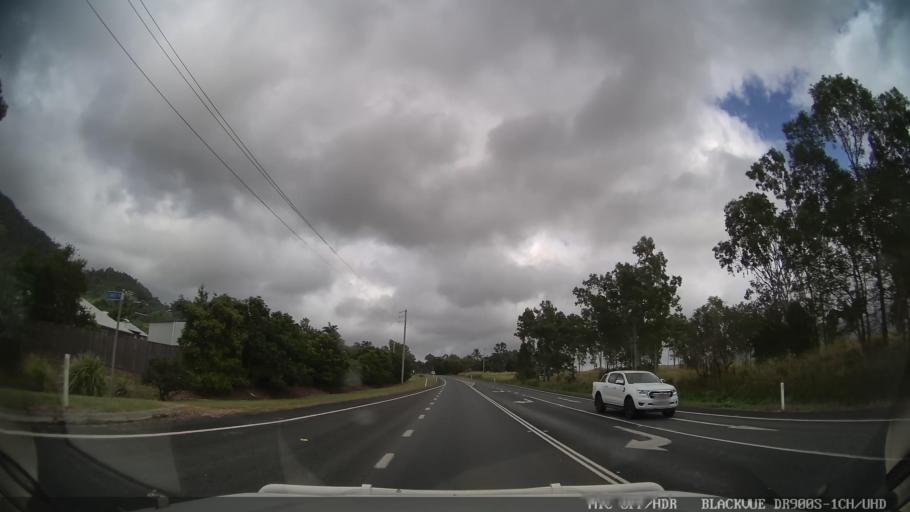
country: AU
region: Queensland
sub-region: Whitsunday
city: Proserpine
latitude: -20.3041
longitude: 148.6651
